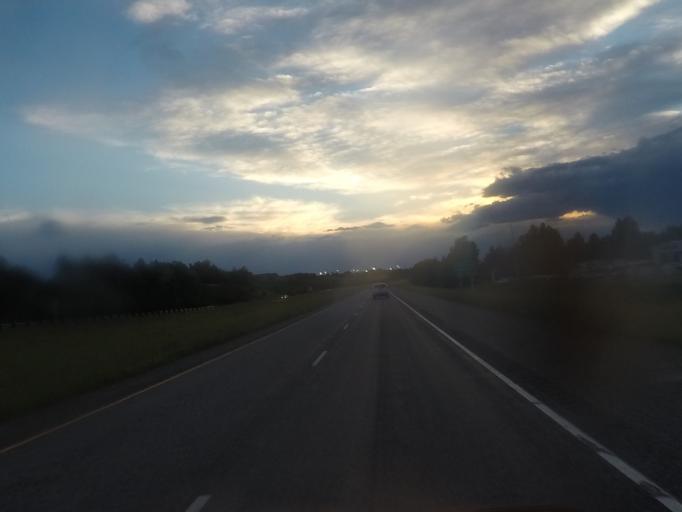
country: US
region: Montana
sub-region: Gallatin County
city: Bozeman
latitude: 45.6716
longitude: -111.0010
